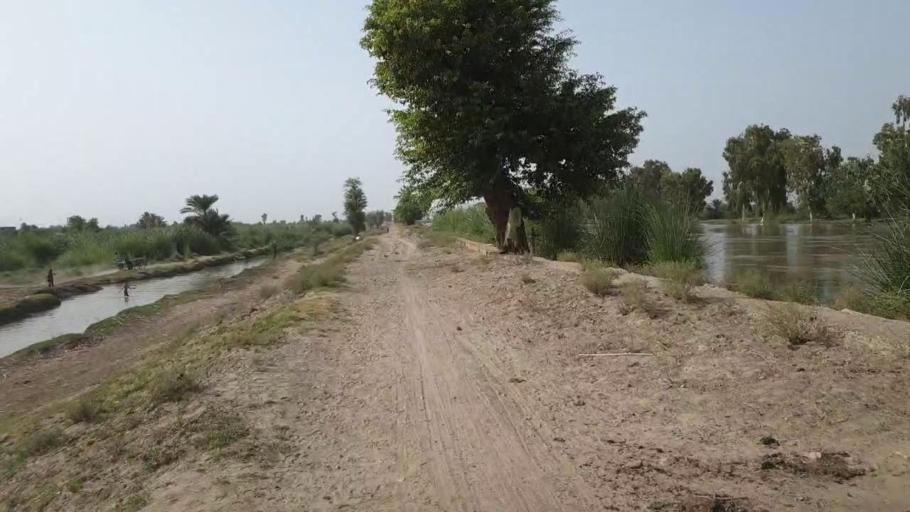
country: PK
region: Sindh
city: Daur
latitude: 26.4514
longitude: 68.1593
